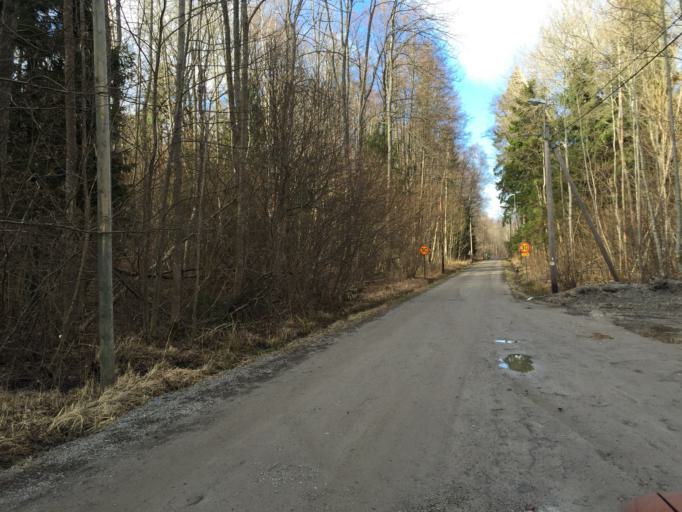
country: SE
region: Stockholm
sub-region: Salems Kommun
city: Ronninge
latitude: 59.1839
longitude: 17.7140
